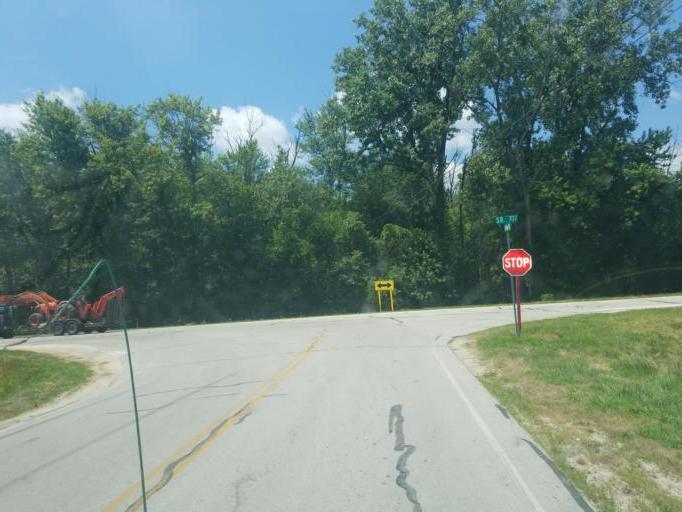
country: US
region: Ohio
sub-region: Mercer County
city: Rockford
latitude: 40.6792
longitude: -84.5184
